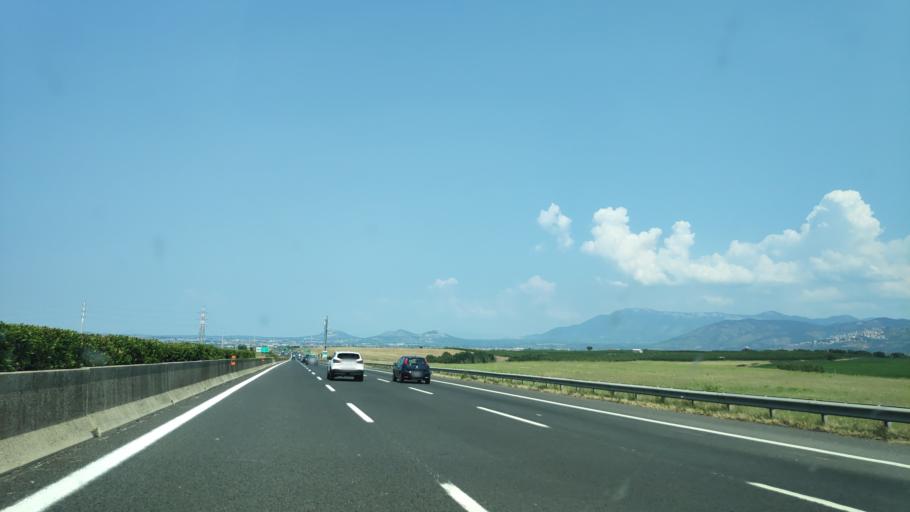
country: IT
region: Latium
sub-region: Citta metropolitana di Roma Capitale
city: Corcolle
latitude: 41.8987
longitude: 12.7541
